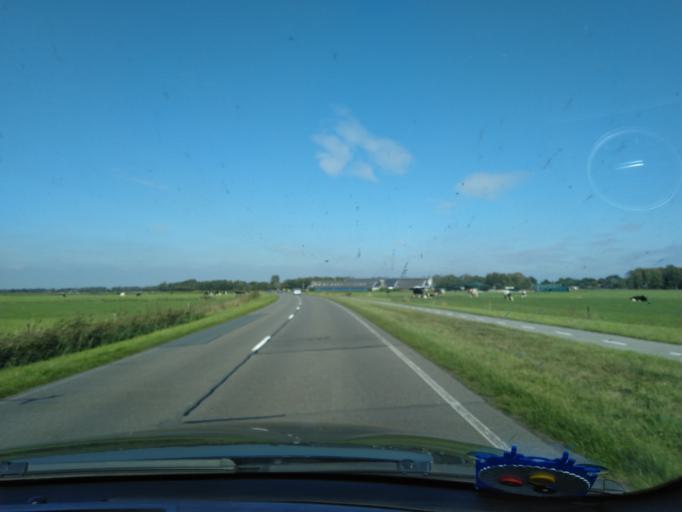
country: NL
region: Drenthe
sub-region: Gemeente Aa en Hunze
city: Anloo
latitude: 53.0674
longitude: 6.7586
